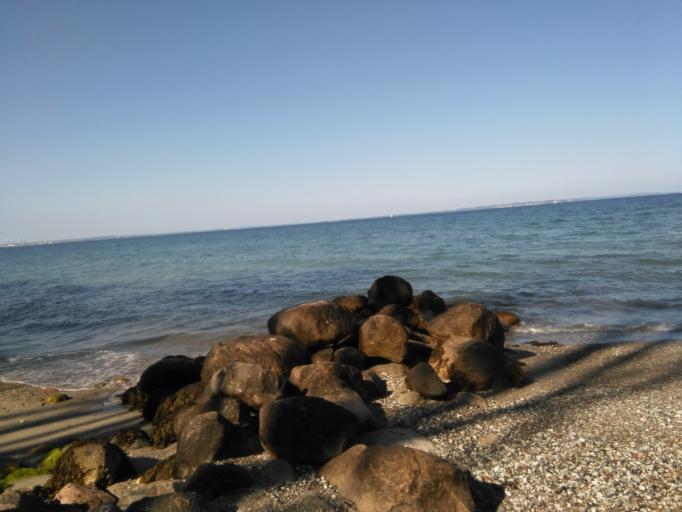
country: DK
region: Central Jutland
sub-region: Arhus Kommune
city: Beder
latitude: 56.0980
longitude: 10.2429
